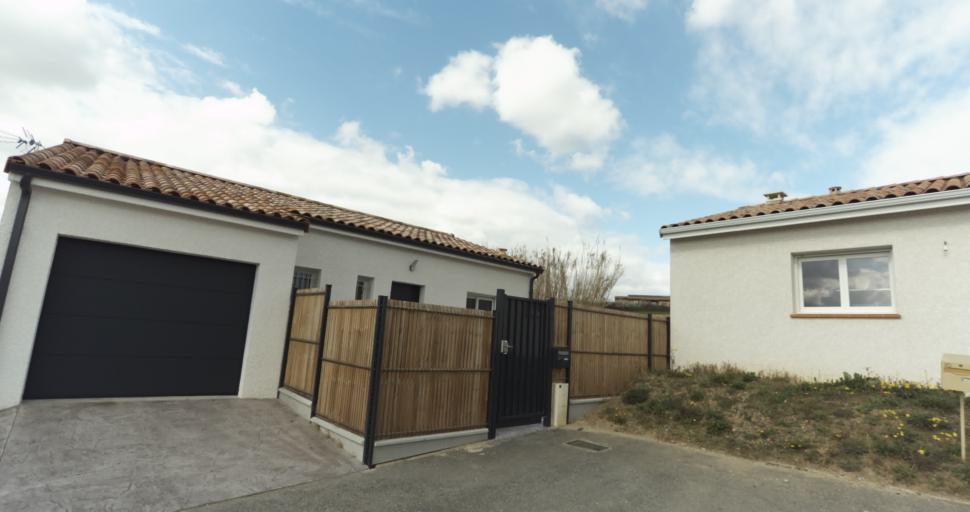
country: FR
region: Midi-Pyrenees
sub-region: Departement de la Haute-Garonne
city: Auterive
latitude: 43.3586
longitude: 1.4806
